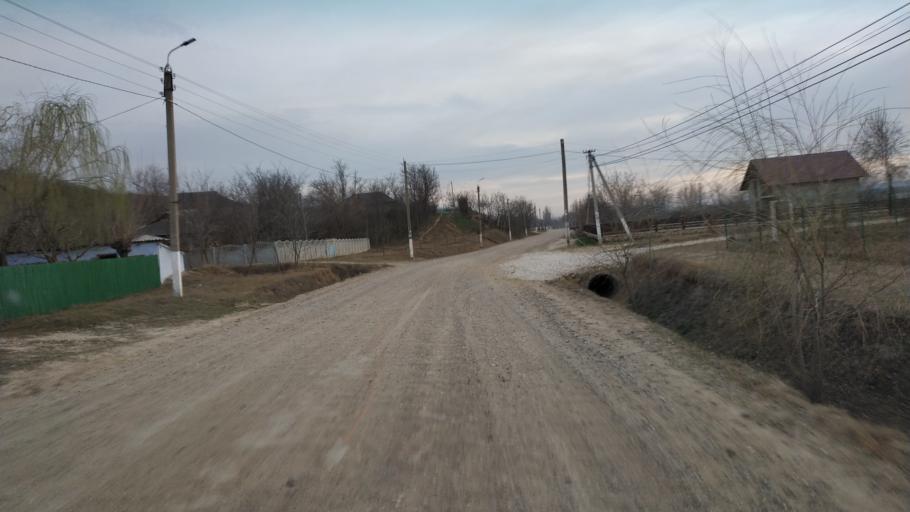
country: MD
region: Hincesti
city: Dancu
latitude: 46.7589
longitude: 28.2089
